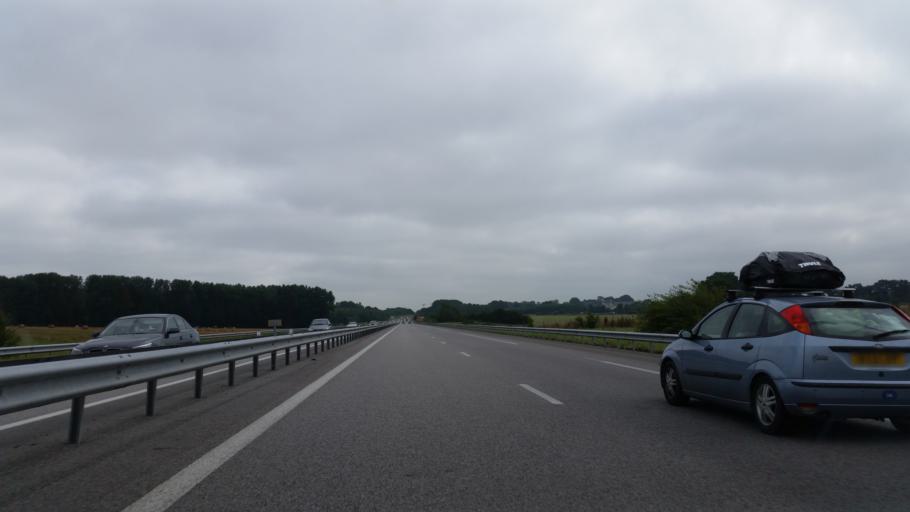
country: FR
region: Haute-Normandie
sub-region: Departement de la Seine-Maritime
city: Totes
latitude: 49.6440
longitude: 0.9911
